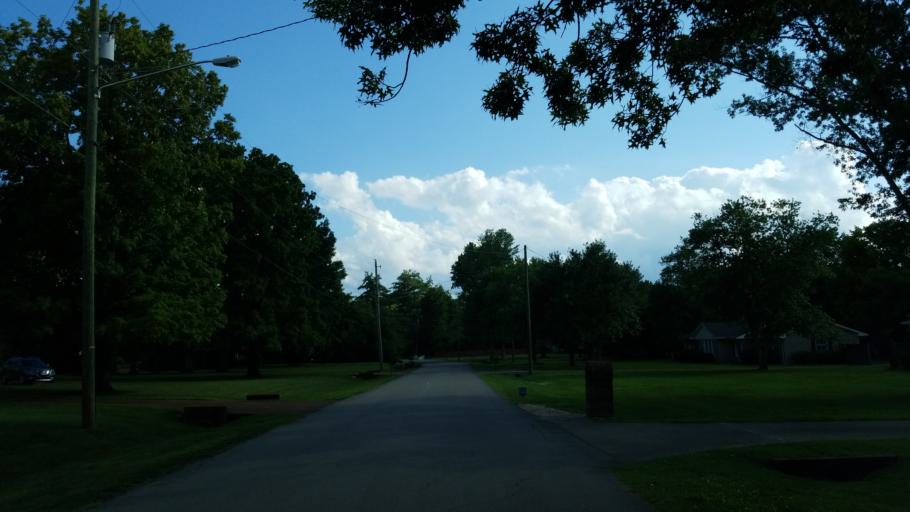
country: US
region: Tennessee
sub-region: Williamson County
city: Brentwood
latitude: 36.0285
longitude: -86.8013
